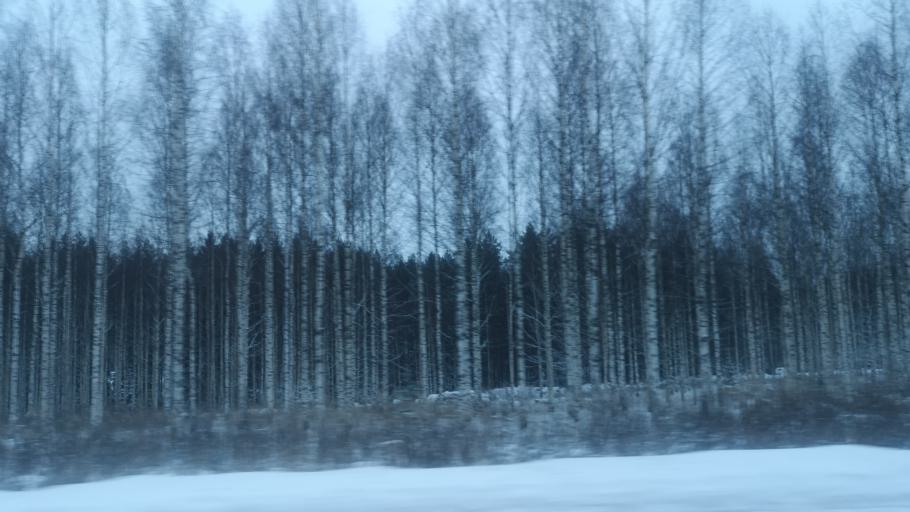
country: FI
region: Southern Savonia
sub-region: Savonlinna
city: Enonkoski
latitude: 62.0708
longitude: 28.7309
